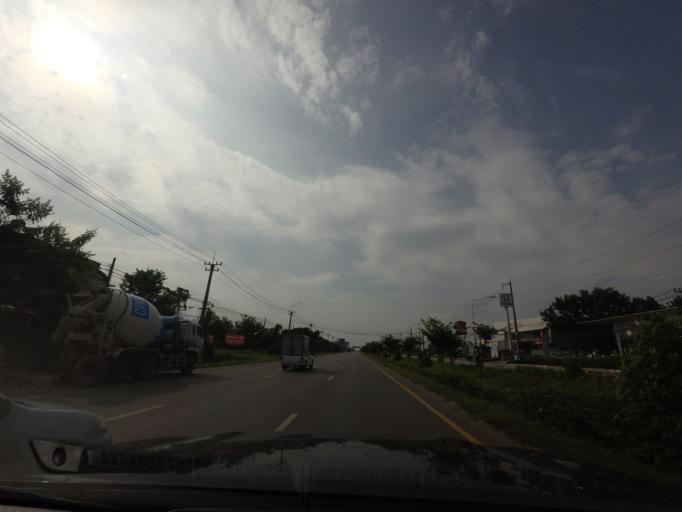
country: TH
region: Nong Khai
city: Nong Khai
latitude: 17.8193
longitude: 102.7578
